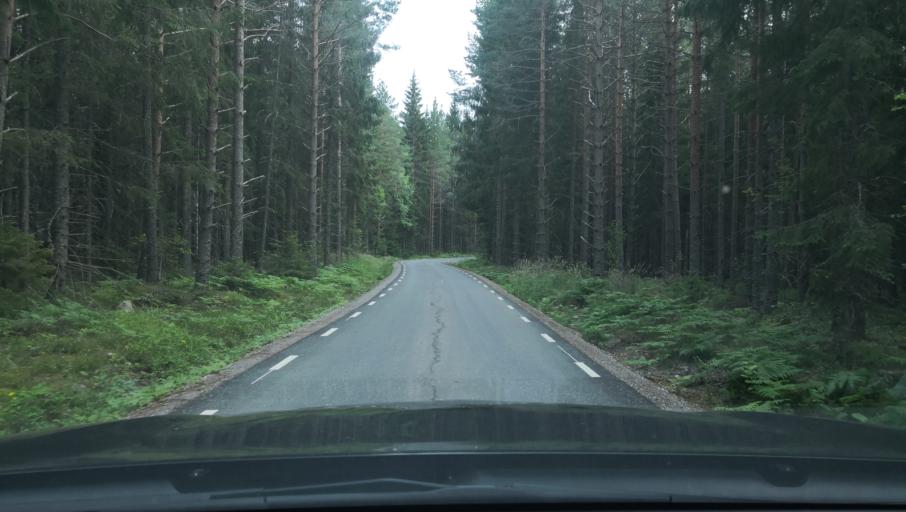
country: SE
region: Vaestmanland
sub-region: Surahammars Kommun
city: Surahammar
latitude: 59.6613
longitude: 16.1322
